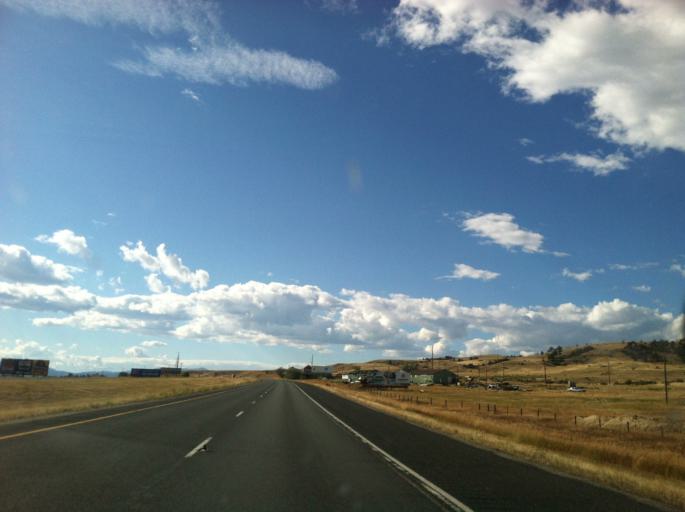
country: US
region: Montana
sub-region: Jefferson County
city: Whitehall
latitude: 45.8726
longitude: -112.0414
